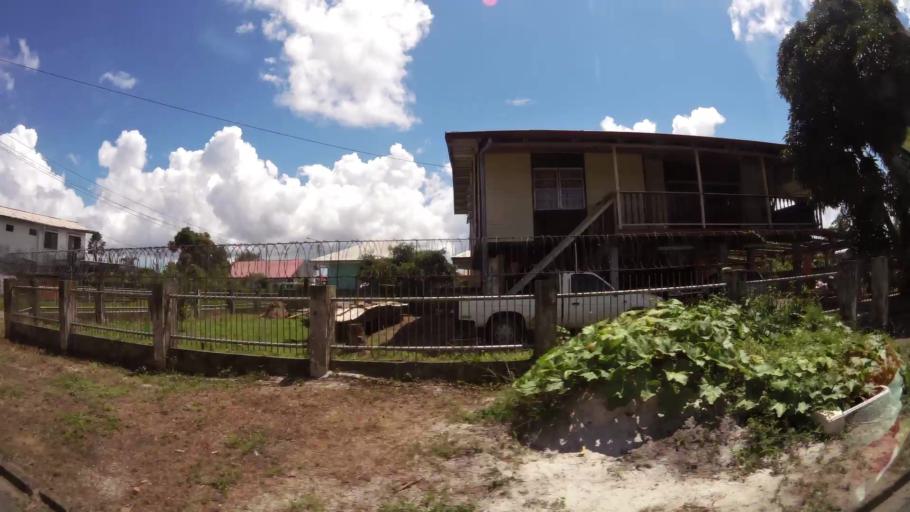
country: SR
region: Paramaribo
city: Paramaribo
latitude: 5.8591
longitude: -55.1447
